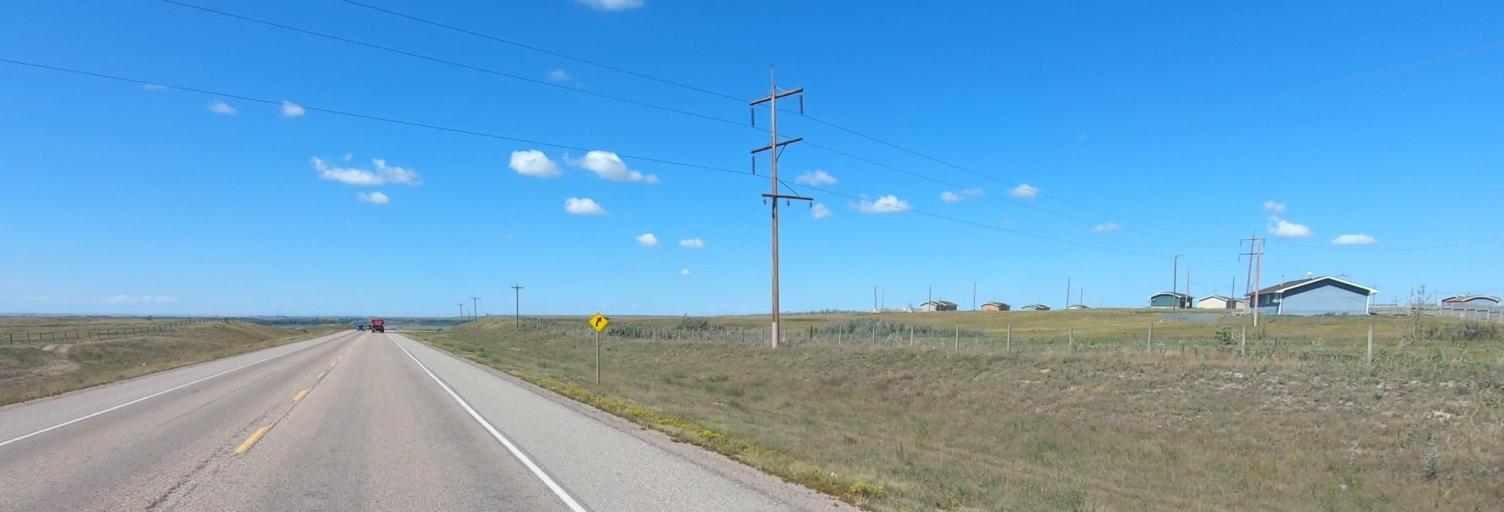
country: CA
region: Alberta
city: Strathmore
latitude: 50.8478
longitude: -113.0781
